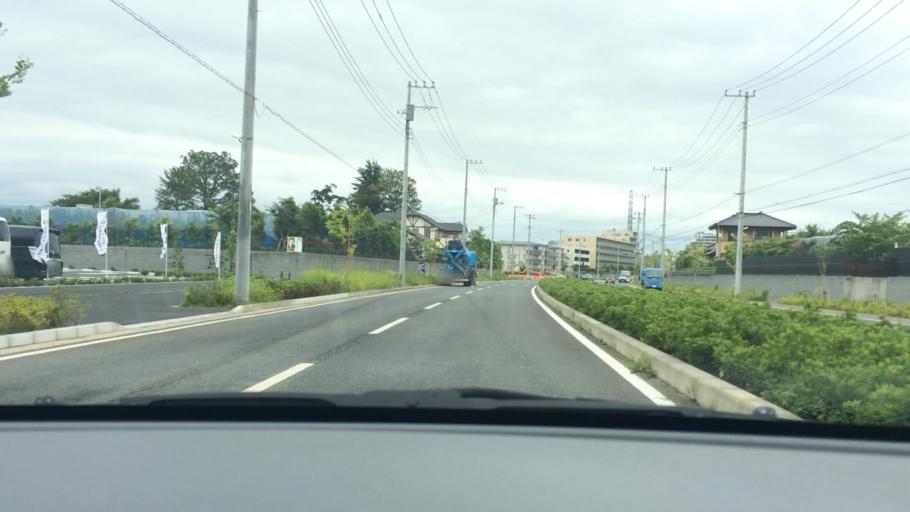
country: JP
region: Chiba
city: Nagareyama
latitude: 35.8757
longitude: 139.9253
